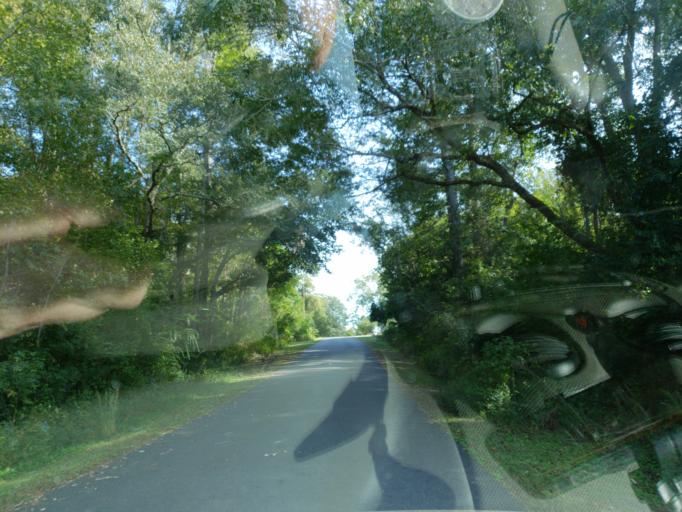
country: US
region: Georgia
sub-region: Crawford County
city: Roberta
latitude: 32.7227
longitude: -84.0079
